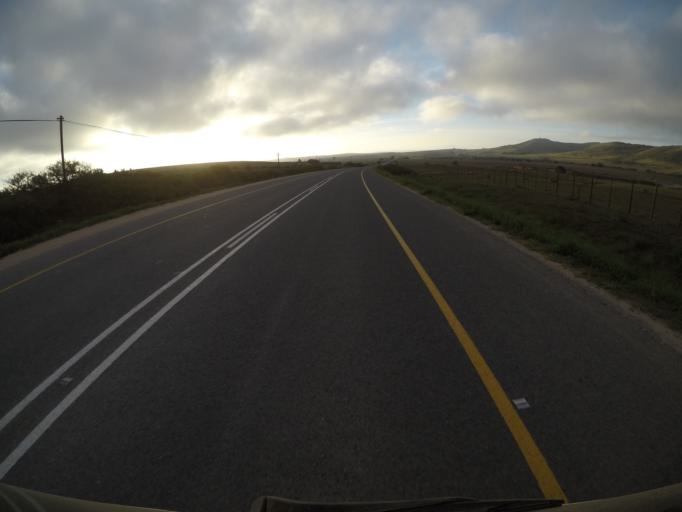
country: ZA
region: Western Cape
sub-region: Eden District Municipality
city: Mossel Bay
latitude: -34.1117
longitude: 22.0766
